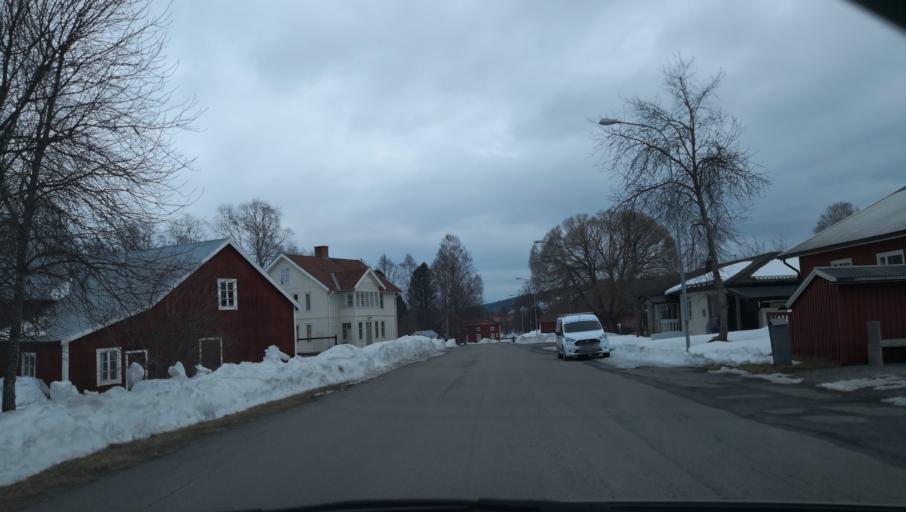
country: SE
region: Vaesterbotten
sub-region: Vannas Kommun
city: Vannasby
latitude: 63.9171
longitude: 19.8137
